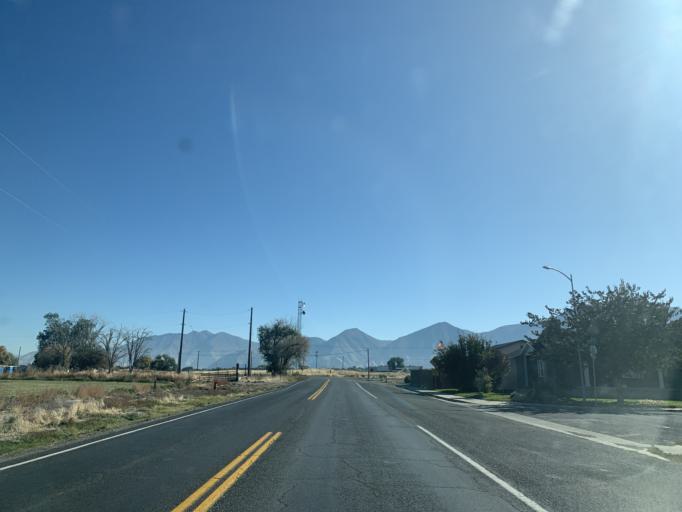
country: US
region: Utah
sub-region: Utah County
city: West Mountain
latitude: 40.0412
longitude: -111.7636
